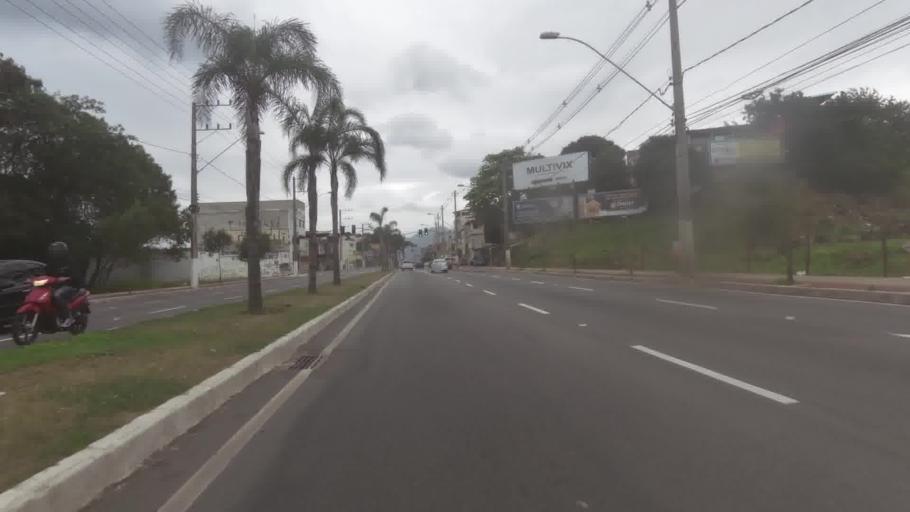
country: BR
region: Espirito Santo
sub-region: Vila Velha
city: Vila Velha
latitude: -20.2726
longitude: -40.3008
